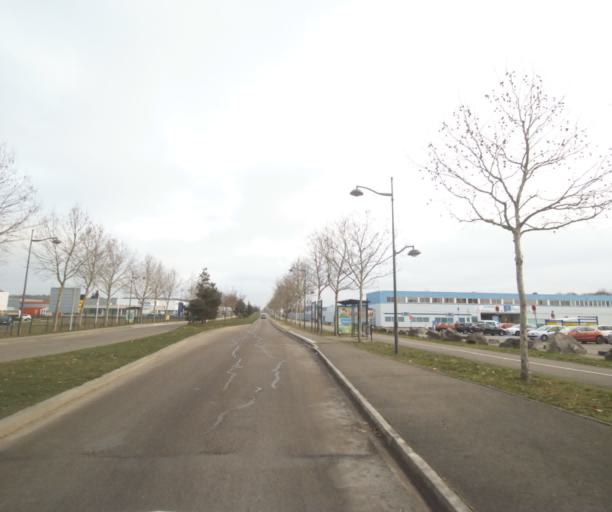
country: FR
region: Champagne-Ardenne
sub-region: Departement de la Haute-Marne
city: Bettancourt-la-Ferree
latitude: 48.6497
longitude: 4.9598
